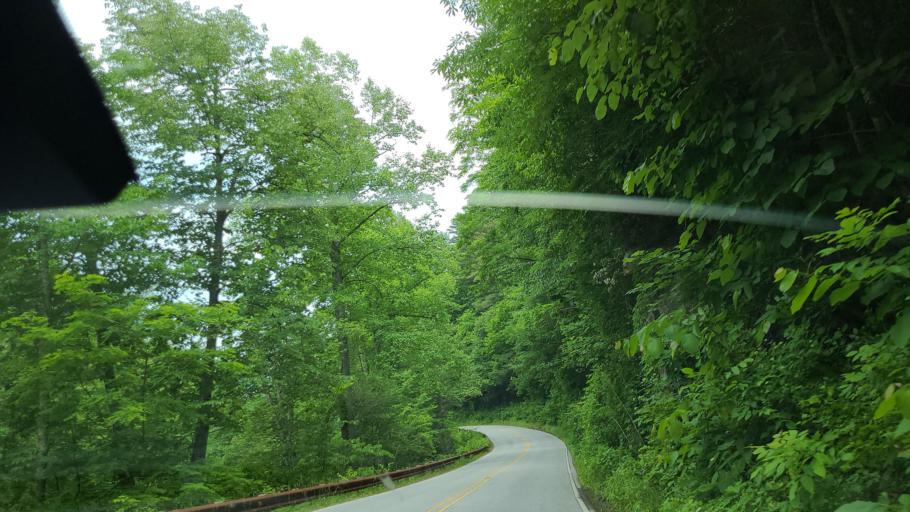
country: US
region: North Carolina
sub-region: Macon County
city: Franklin
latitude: 35.1141
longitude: -83.2657
